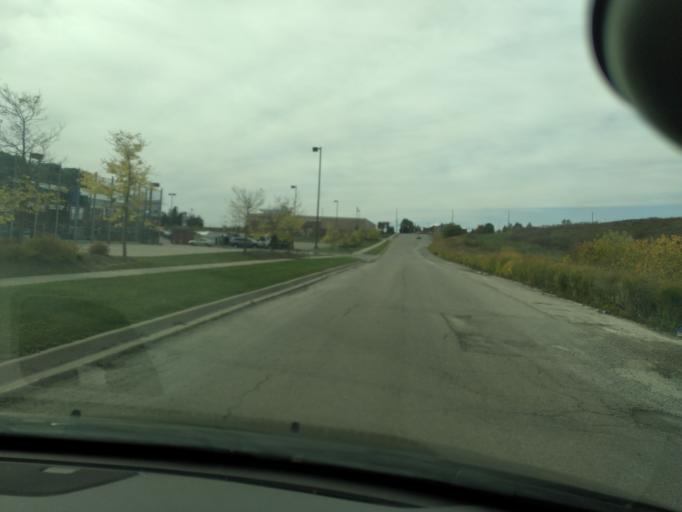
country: CA
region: Ontario
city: Newmarket
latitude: 44.0778
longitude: -79.4815
